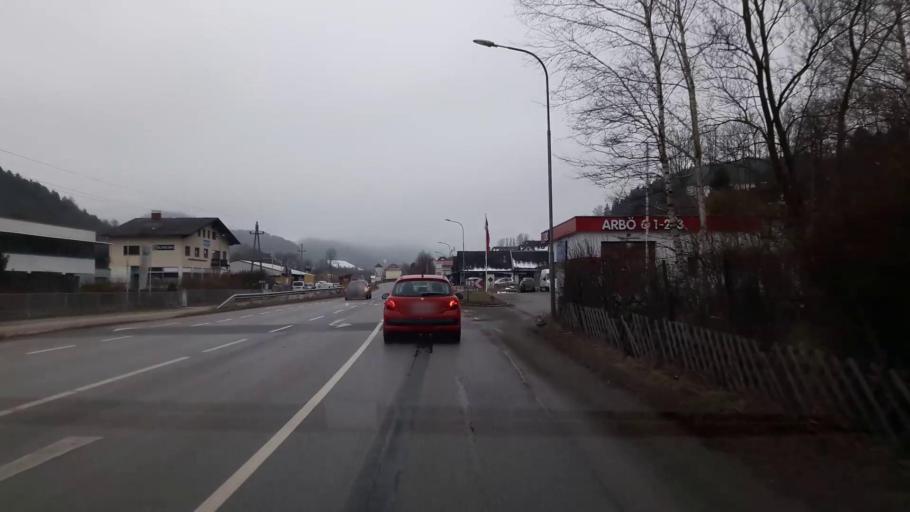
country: AT
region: Lower Austria
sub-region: Politischer Bezirk Neunkirchen
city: Edlitz
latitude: 47.5822
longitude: 16.0998
